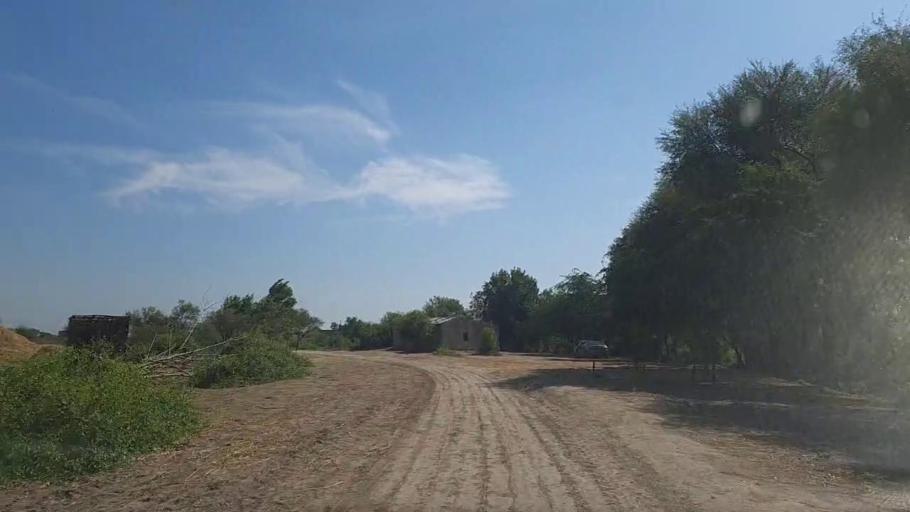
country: PK
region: Sindh
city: Mirpur Batoro
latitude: 24.7593
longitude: 68.2979
